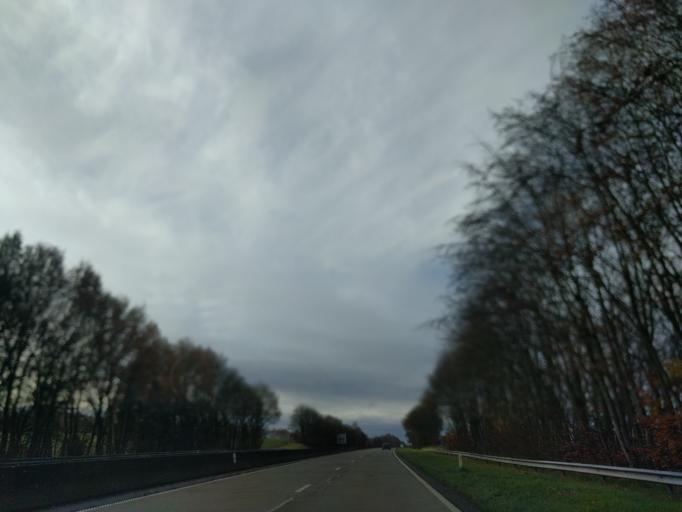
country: BE
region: Wallonia
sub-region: Province de Namur
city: Houyet
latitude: 50.2554
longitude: 5.0208
